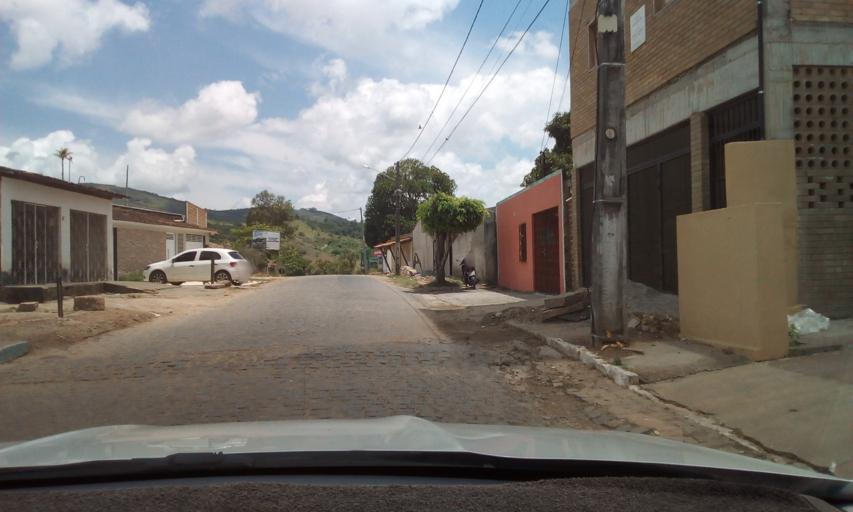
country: BR
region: Pernambuco
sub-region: Bonito
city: Bonito
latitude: -8.4785
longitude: -35.7290
